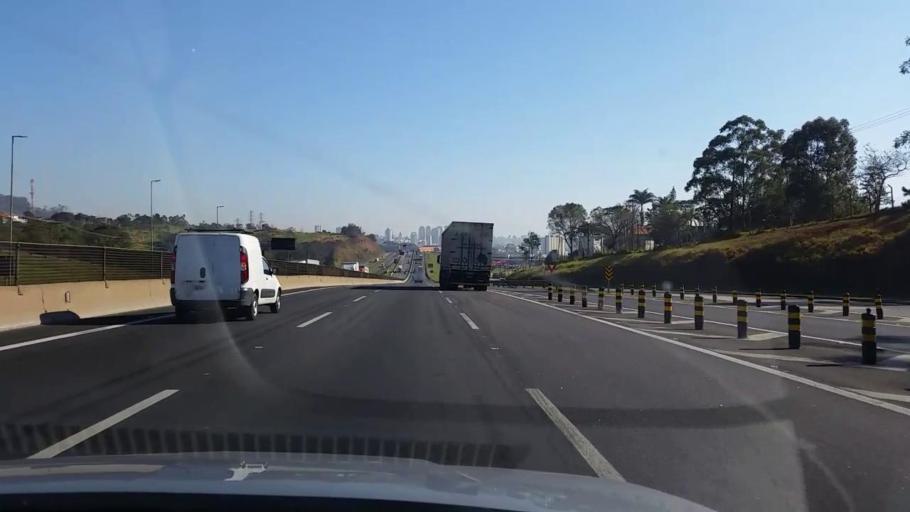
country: BR
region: Sao Paulo
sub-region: Jundiai
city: Jundiai
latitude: -23.2332
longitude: -46.8716
